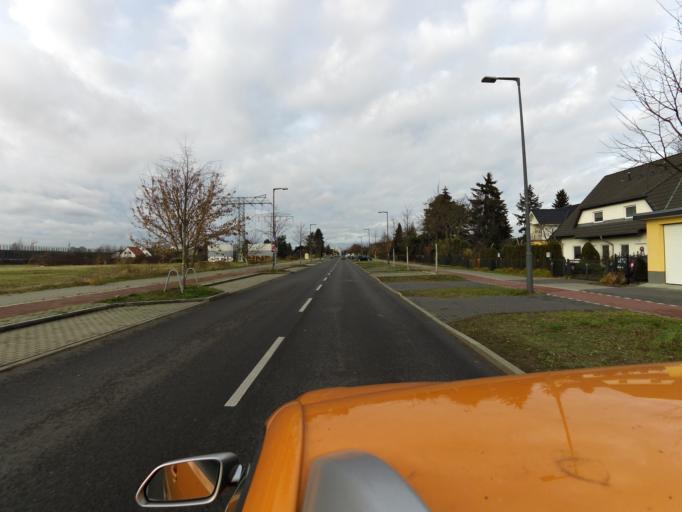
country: DE
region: Berlin
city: Johannisthal
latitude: 52.4305
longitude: 13.5086
